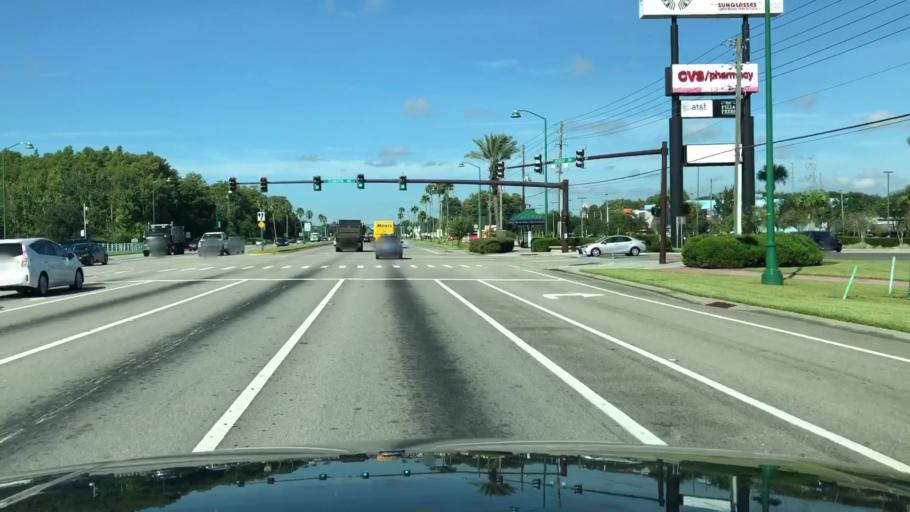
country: US
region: Florida
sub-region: Osceola County
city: Celebration
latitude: 28.3329
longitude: -81.5274
